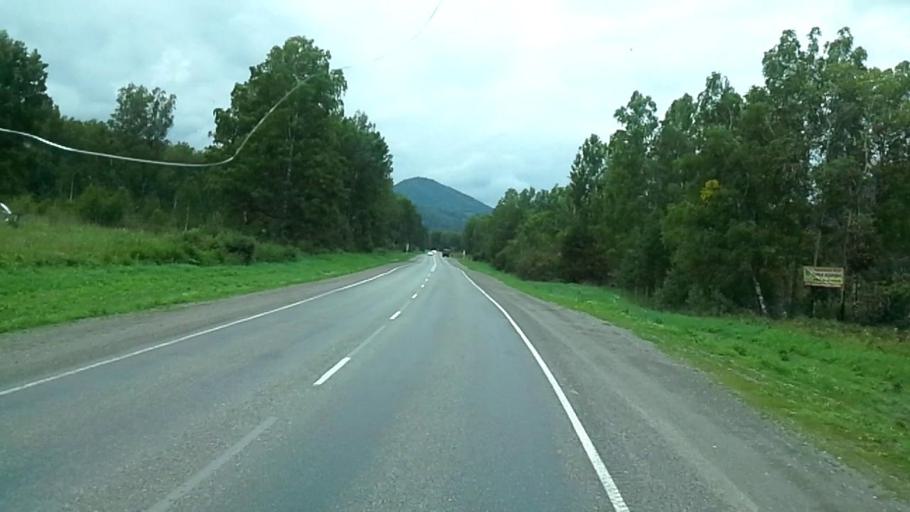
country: RU
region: Altay
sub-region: Mayminskiy Rayon
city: Manzherok
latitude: 51.8546
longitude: 85.7458
